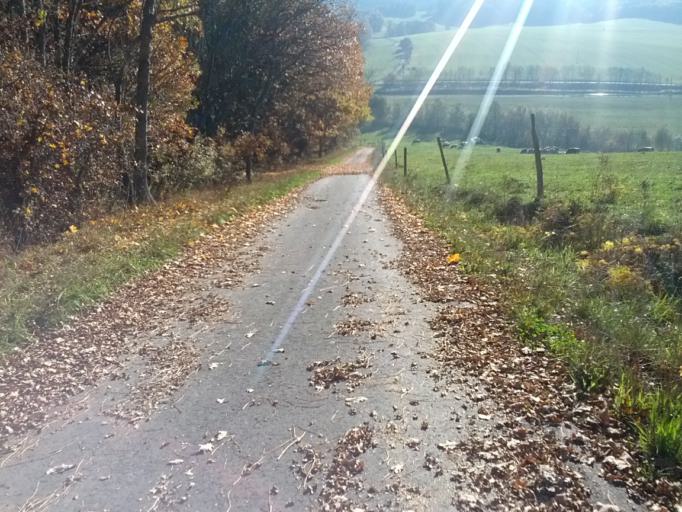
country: DE
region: Thuringia
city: Seebach
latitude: 50.9465
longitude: 10.4537
